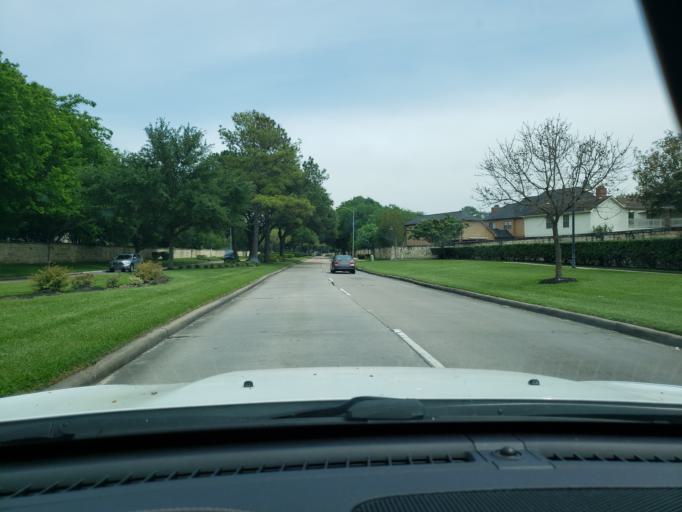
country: US
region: Texas
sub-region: Harris County
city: Jersey Village
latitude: 29.9093
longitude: -95.5772
